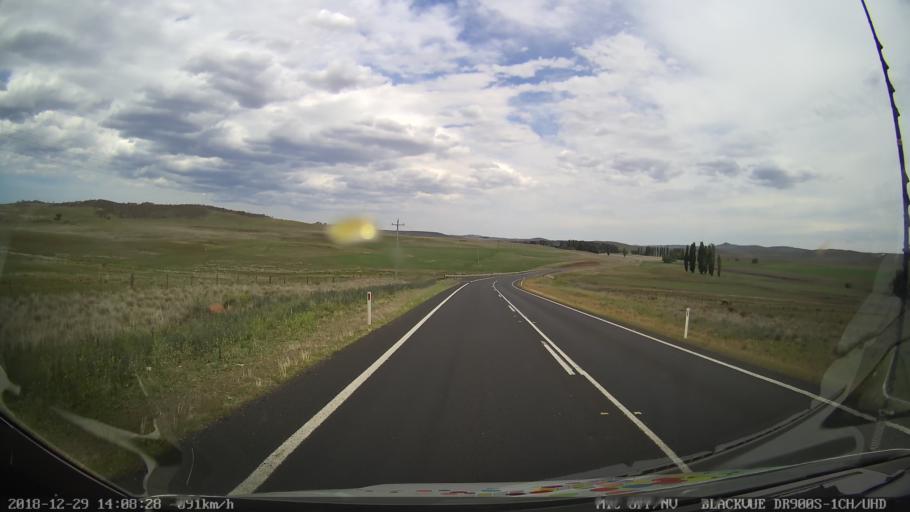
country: AU
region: New South Wales
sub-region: Cooma-Monaro
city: Cooma
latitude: -36.3656
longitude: 149.2145
